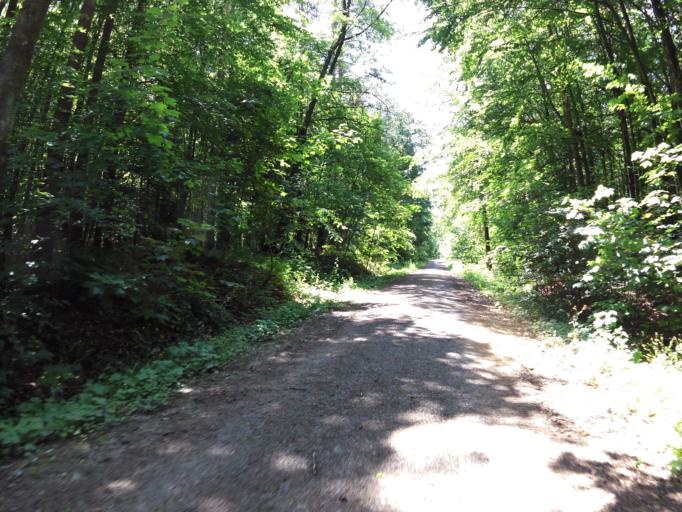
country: DE
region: Bavaria
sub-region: Regierungsbezirk Unterfranken
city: Kleinrinderfeld
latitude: 49.7210
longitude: 9.8522
